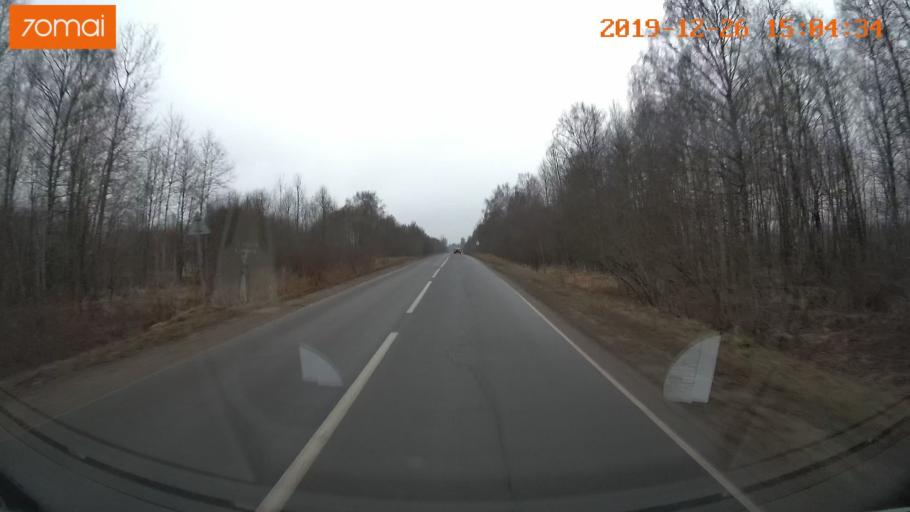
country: RU
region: Jaroslavl
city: Rybinsk
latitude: 58.1983
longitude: 38.8604
